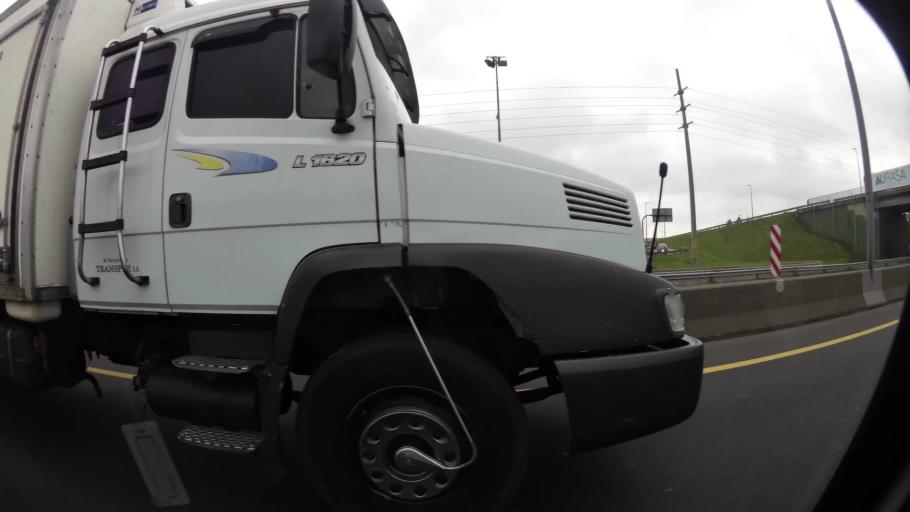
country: AR
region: Buenos Aires
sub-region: Partido de Quilmes
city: Quilmes
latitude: -34.7018
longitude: -58.2742
